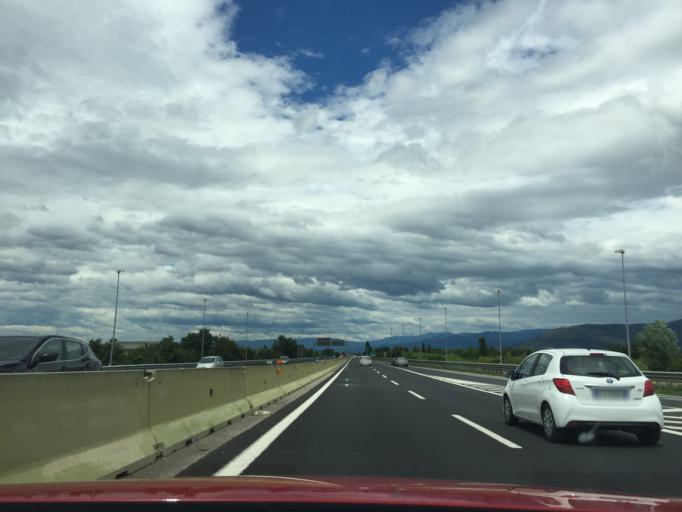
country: IT
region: Tuscany
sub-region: Province of Florence
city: Sesto Fiorentino
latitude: 43.8138
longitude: 11.1811
